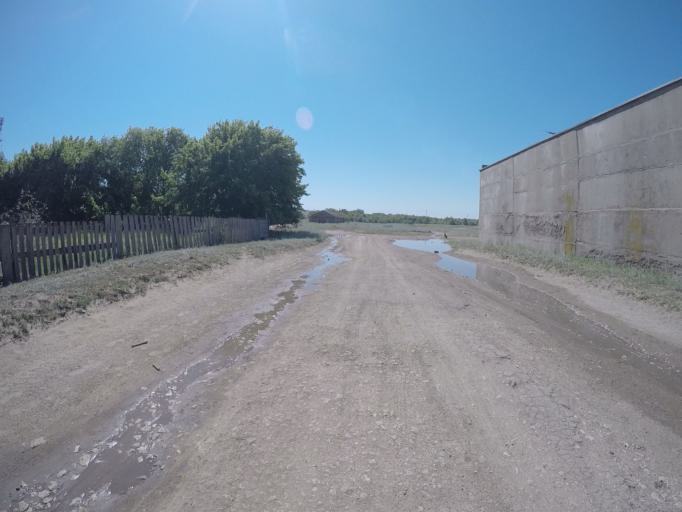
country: RU
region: Saratov
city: Privolzhskiy
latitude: 51.1760
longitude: 45.9219
